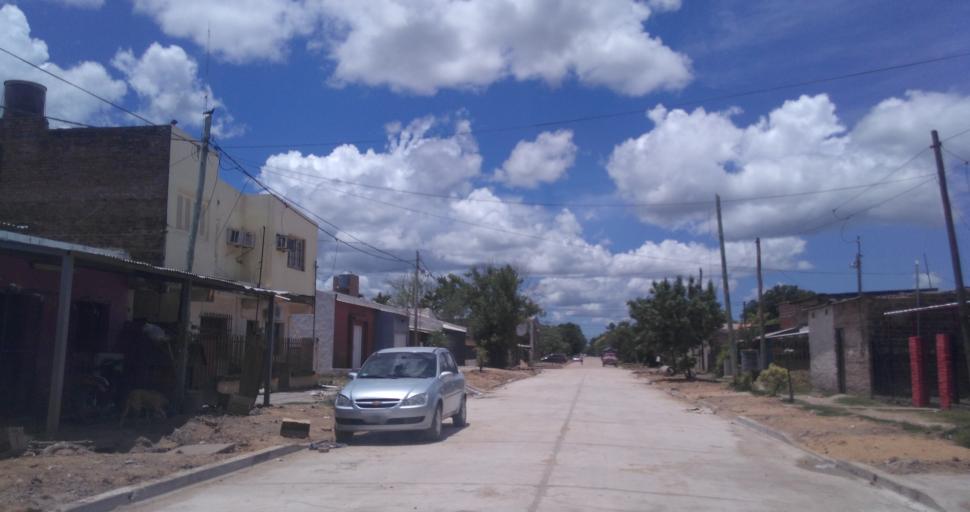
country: AR
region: Chaco
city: Resistencia
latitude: -27.4396
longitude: -58.9754
